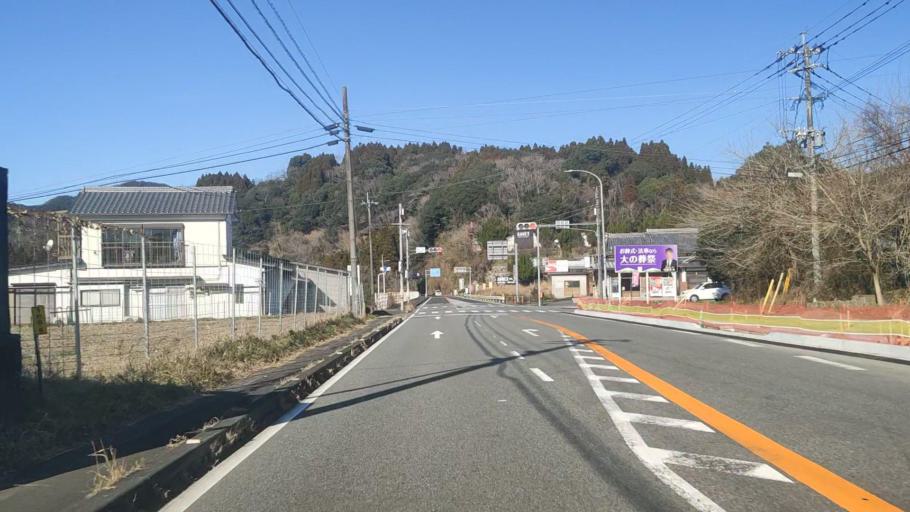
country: JP
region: Oita
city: Usuki
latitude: 33.0518
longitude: 131.6890
